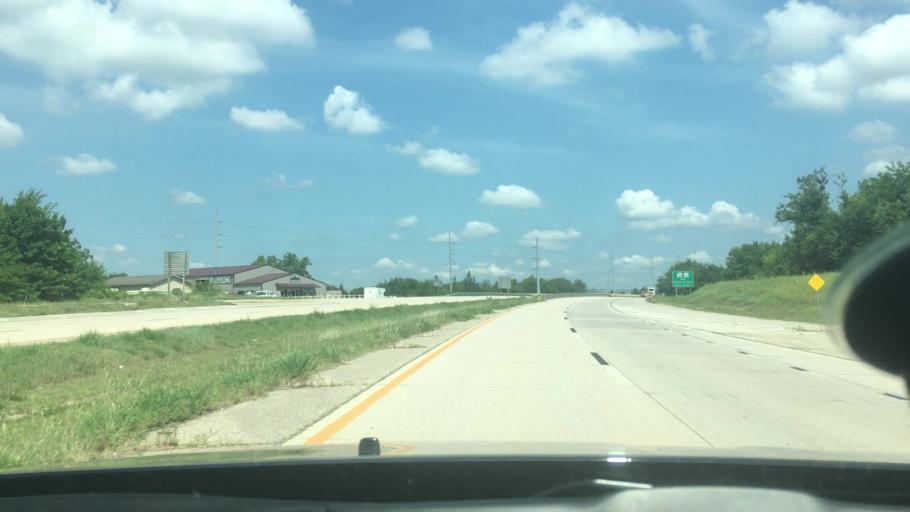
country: US
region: Oklahoma
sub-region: Pontotoc County
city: Ada
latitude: 34.7652
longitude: -96.7033
